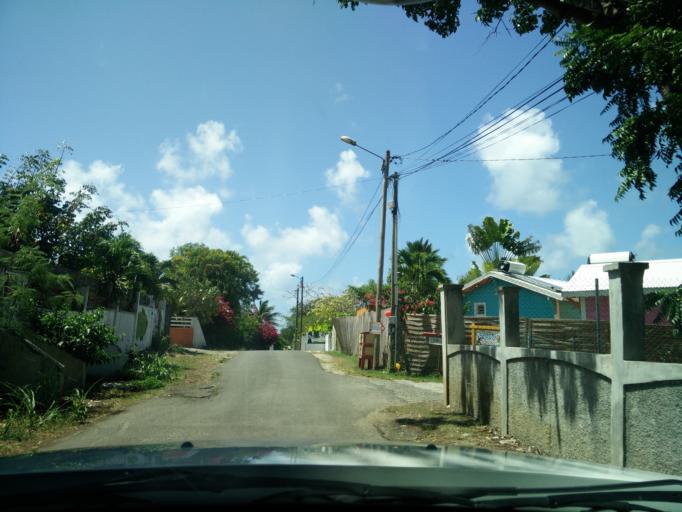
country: GP
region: Guadeloupe
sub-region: Guadeloupe
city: Sainte-Anne
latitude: 16.2452
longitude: -61.3427
